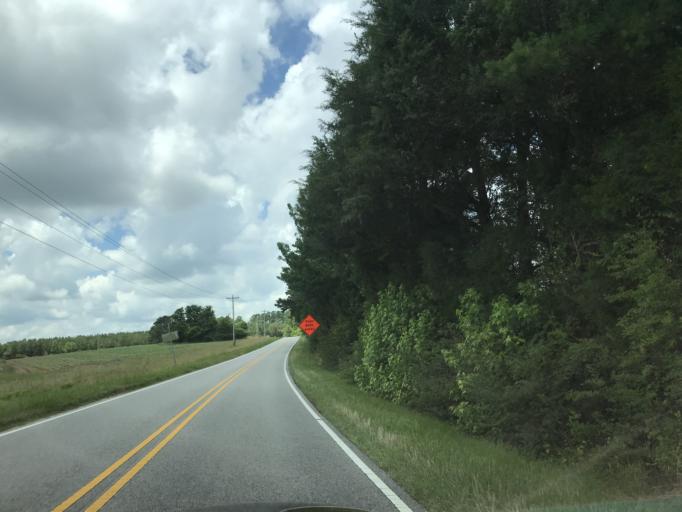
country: US
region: North Carolina
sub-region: Wake County
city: Rolesville
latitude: 35.9606
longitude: -78.4015
